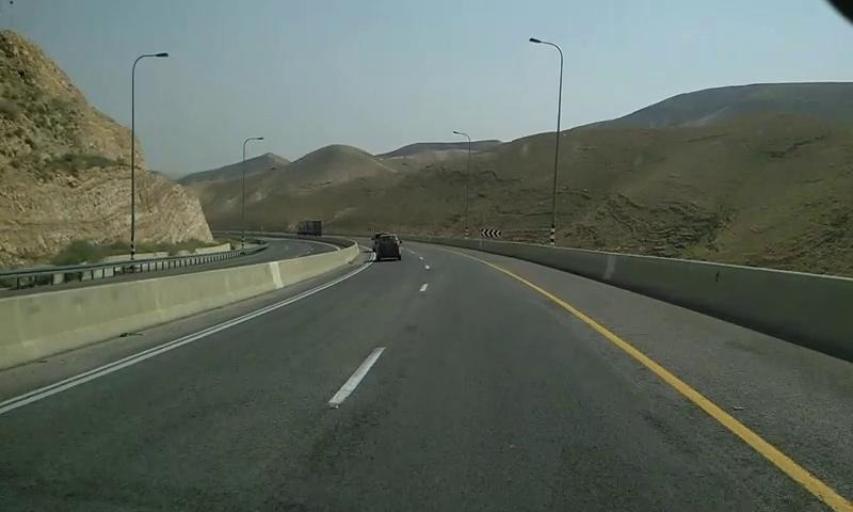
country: PS
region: West Bank
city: Jericho
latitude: 31.8103
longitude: 35.3909
